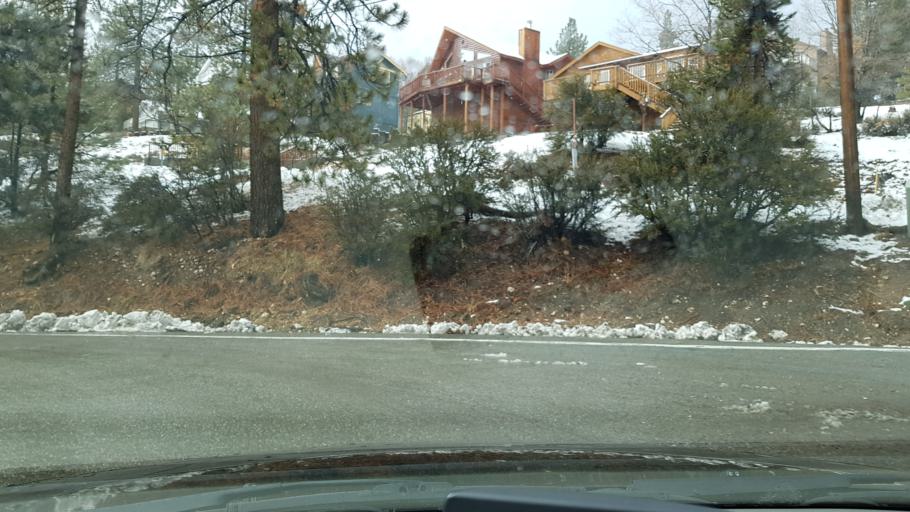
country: US
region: California
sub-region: San Bernardino County
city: Big Bear Lake
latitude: 34.2678
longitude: -116.9430
